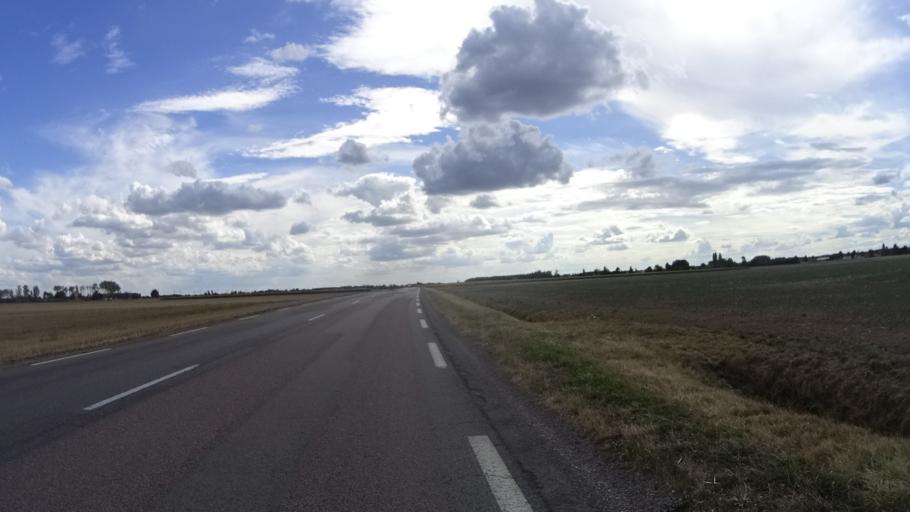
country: FR
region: Bourgogne
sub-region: Departement de la Cote-d'Or
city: Seurre
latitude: 47.0236
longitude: 5.1682
